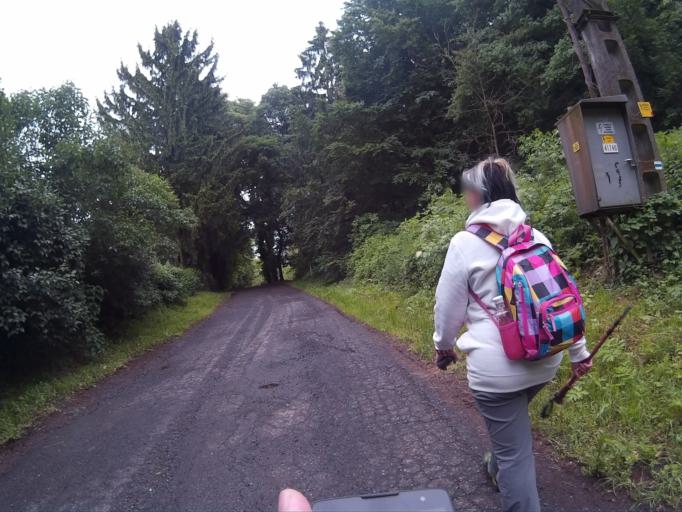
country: HU
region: Veszprem
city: Sumeg
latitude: 46.9351
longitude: 17.2917
